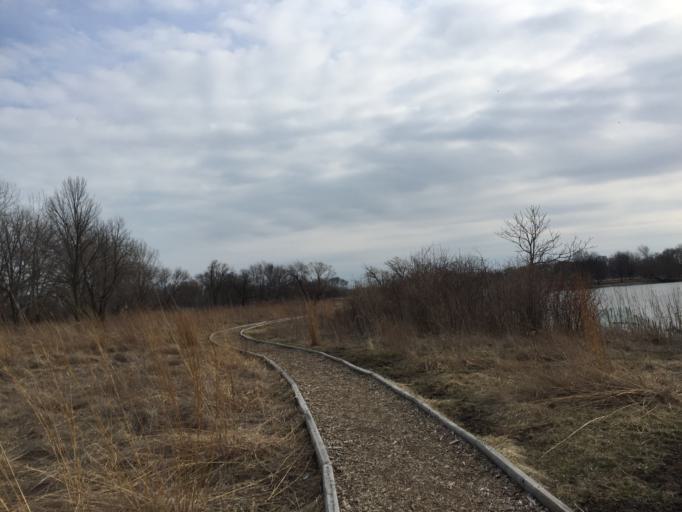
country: US
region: Illinois
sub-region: Cook County
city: Chicago
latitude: 41.7851
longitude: -87.5806
